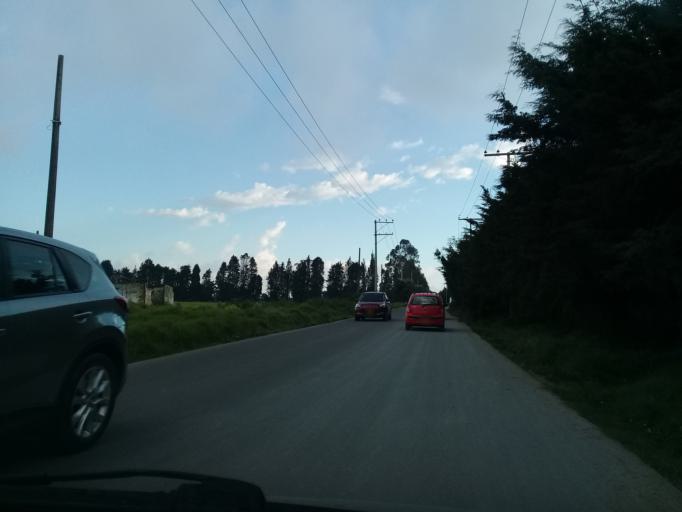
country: CO
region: Cundinamarca
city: Madrid
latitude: 4.7707
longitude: -74.2667
